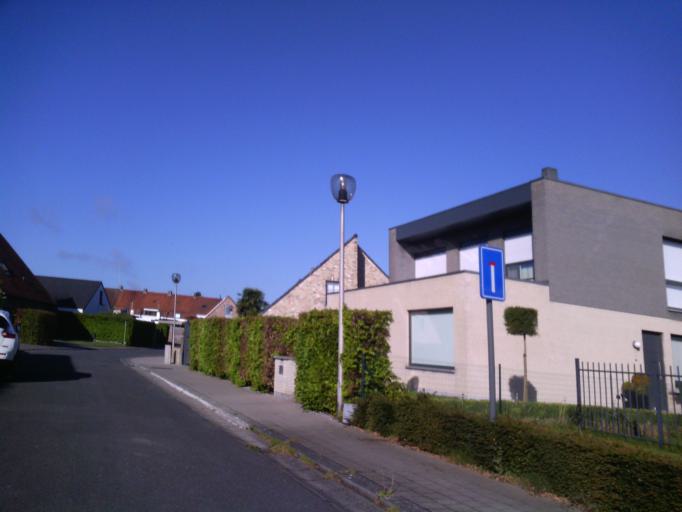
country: BE
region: Flanders
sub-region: Provincie West-Vlaanderen
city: Wevelgem
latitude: 50.7779
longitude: 3.1791
